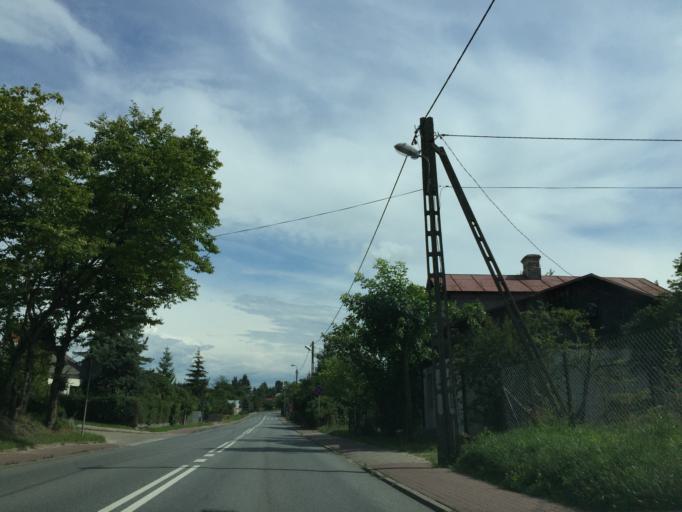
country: PL
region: Masovian Voivodeship
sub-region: Powiat losicki
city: Sarnaki
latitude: 52.3180
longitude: 22.8860
